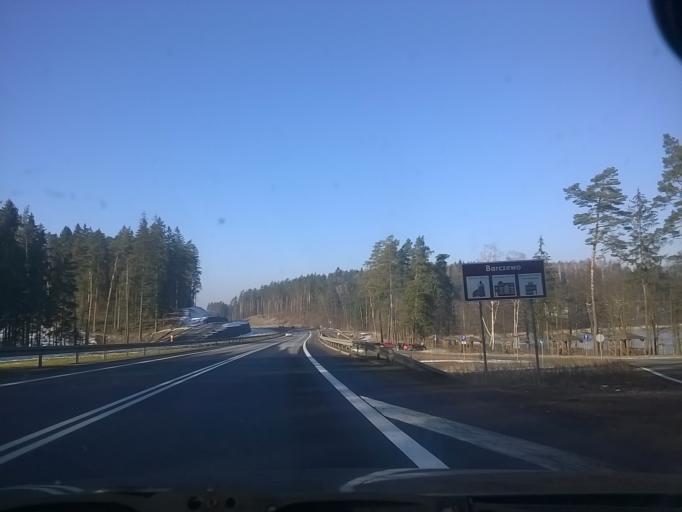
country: PL
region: Warmian-Masurian Voivodeship
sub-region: Powiat olsztynski
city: Barczewo
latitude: 53.8318
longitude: 20.7743
